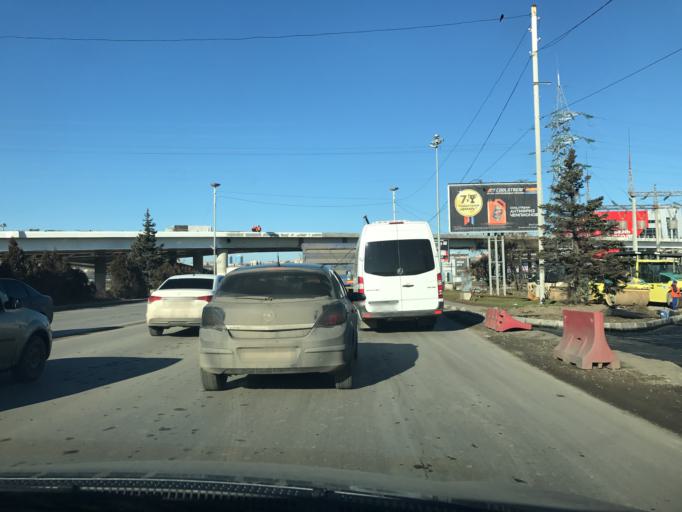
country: RU
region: Rostov
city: Rostov-na-Donu
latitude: 47.2030
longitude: 39.7278
